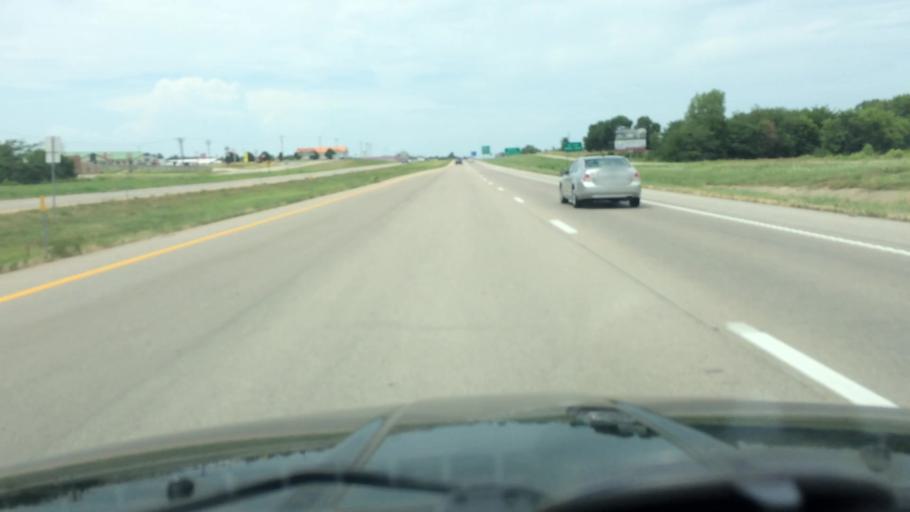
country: US
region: Missouri
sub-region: Polk County
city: Bolivar
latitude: 37.5544
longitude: -93.3879
